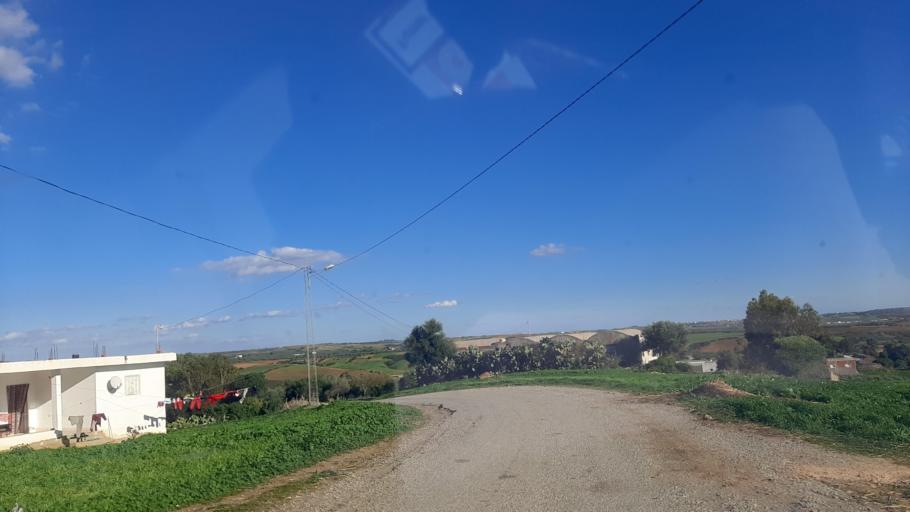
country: TN
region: Nabul
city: El Mida
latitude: 36.8388
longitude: 10.8279
